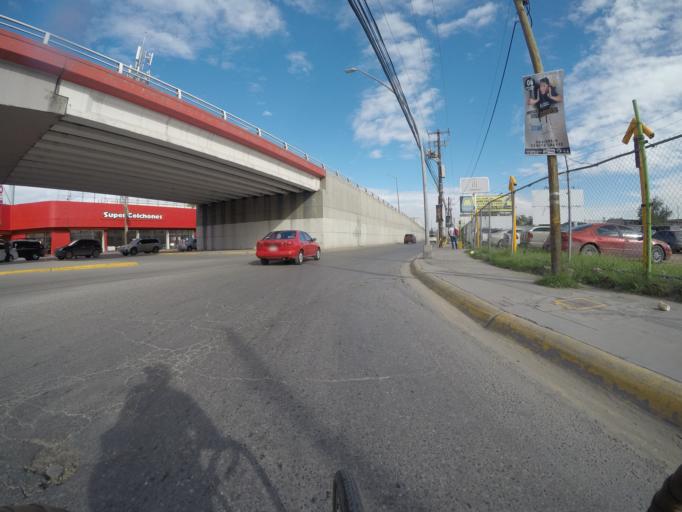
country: MX
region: Chihuahua
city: Ciudad Juarez
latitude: 31.7245
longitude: -106.4243
